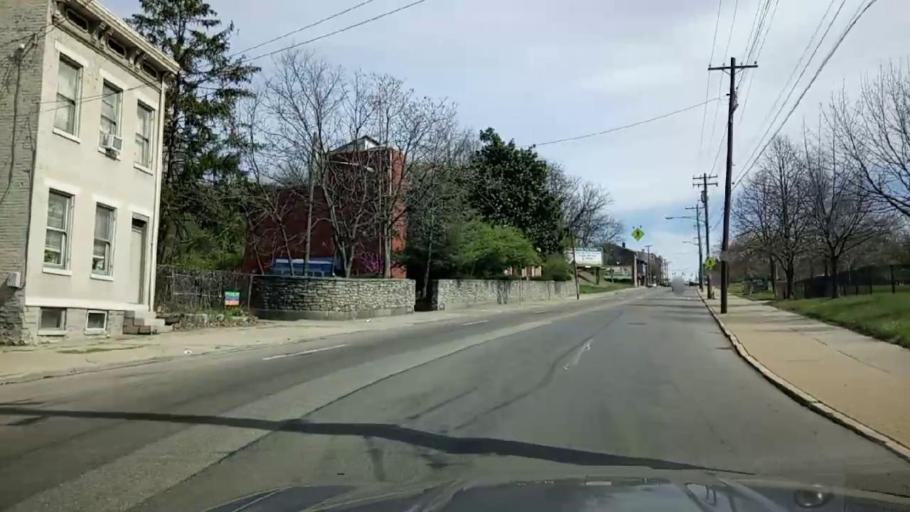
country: US
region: Kentucky
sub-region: Campbell County
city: Newport
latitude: 39.1245
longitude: -84.5142
